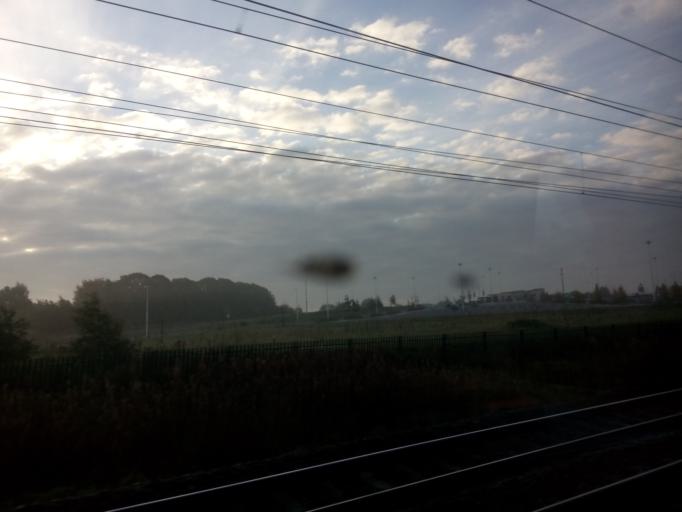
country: GB
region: England
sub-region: City of York
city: Bishopthorpe
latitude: 53.9311
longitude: -1.1182
